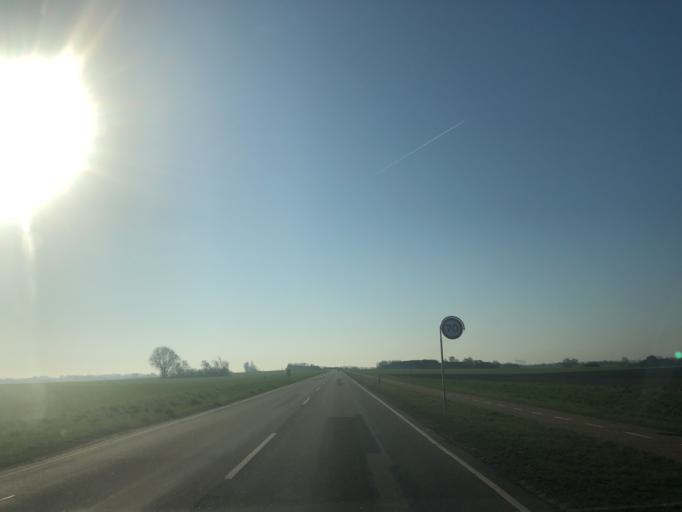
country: DK
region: Zealand
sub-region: Ringsted Kommune
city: Ringsted
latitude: 55.3713
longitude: 11.8605
